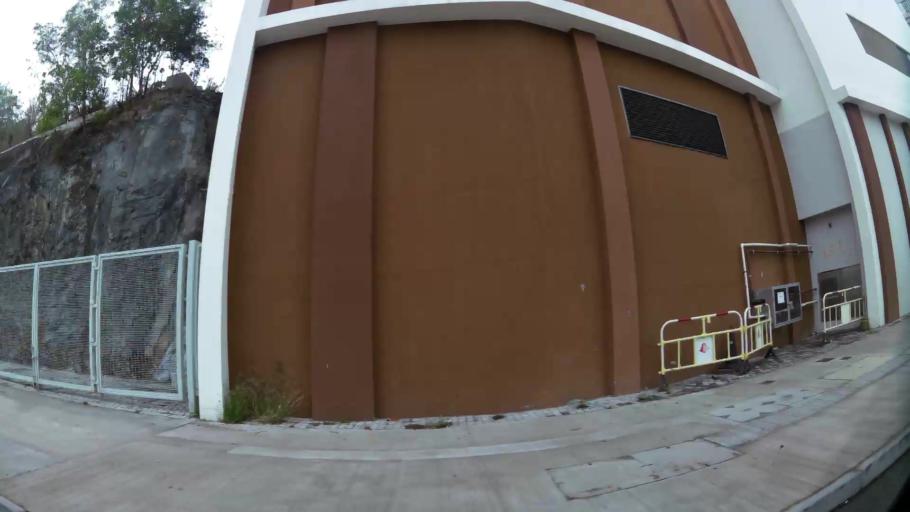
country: HK
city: Sok Kwu Wan
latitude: 22.2394
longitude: 114.1515
